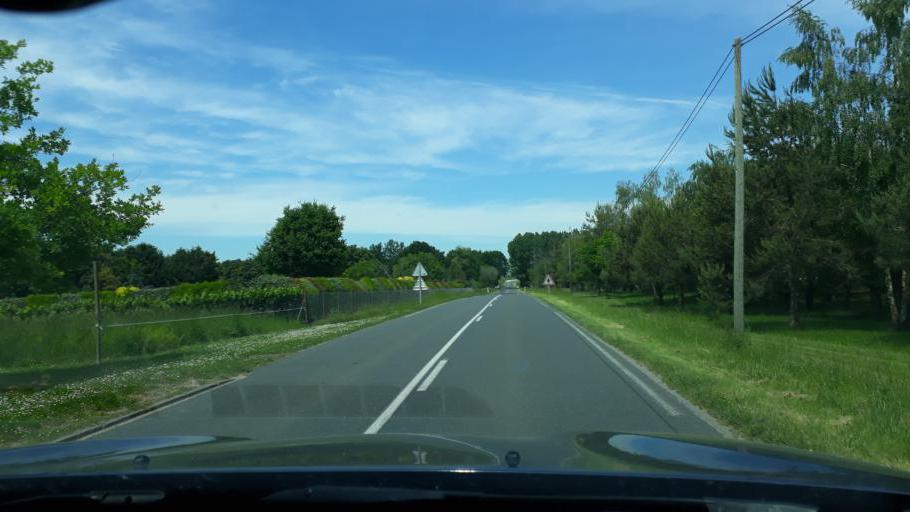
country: FR
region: Centre
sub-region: Departement du Loiret
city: Boynes
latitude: 48.0667
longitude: 2.2862
